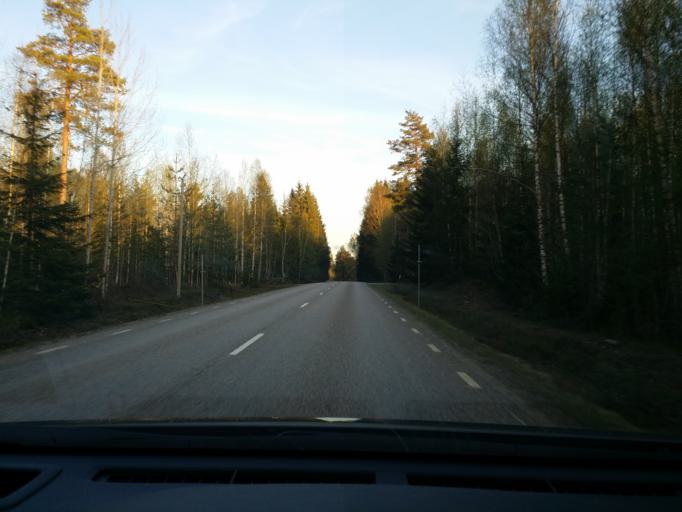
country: SE
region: Vaestmanland
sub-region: Sala Kommun
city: Sala
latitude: 59.8352
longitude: 16.5038
